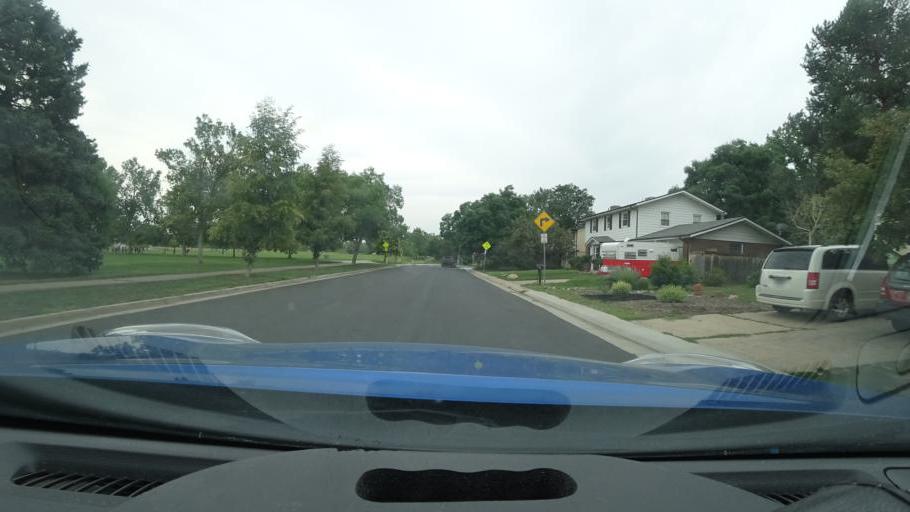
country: US
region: Colorado
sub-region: Arapahoe County
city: Glendale
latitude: 39.6858
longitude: -104.9092
